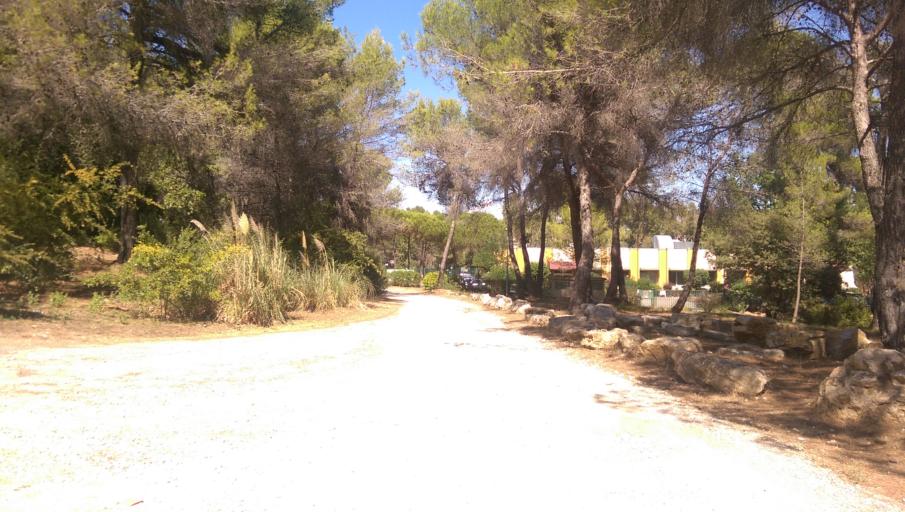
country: FR
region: Provence-Alpes-Cote d'Azur
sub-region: Departement des Alpes-Maritimes
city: Valbonne
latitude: 43.6248
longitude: 7.0417
